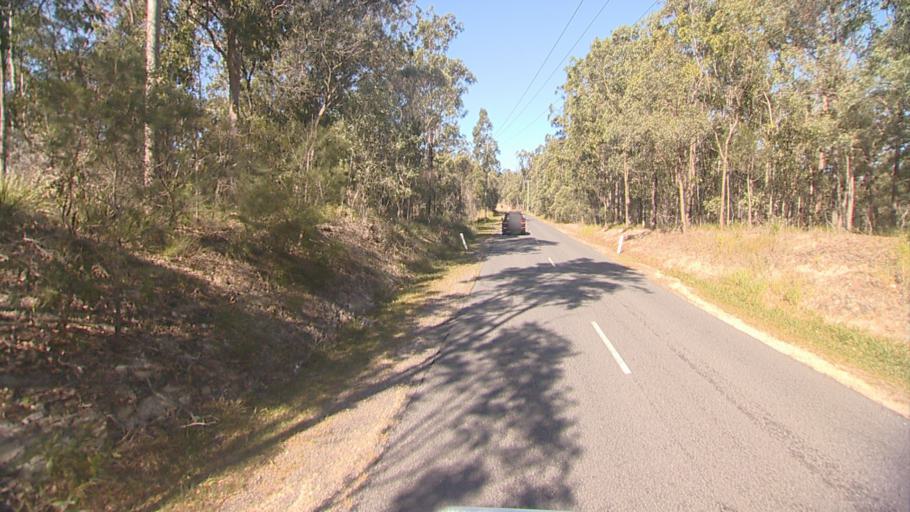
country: AU
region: Queensland
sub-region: Logan
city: Springwood
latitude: -27.6083
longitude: 153.1791
